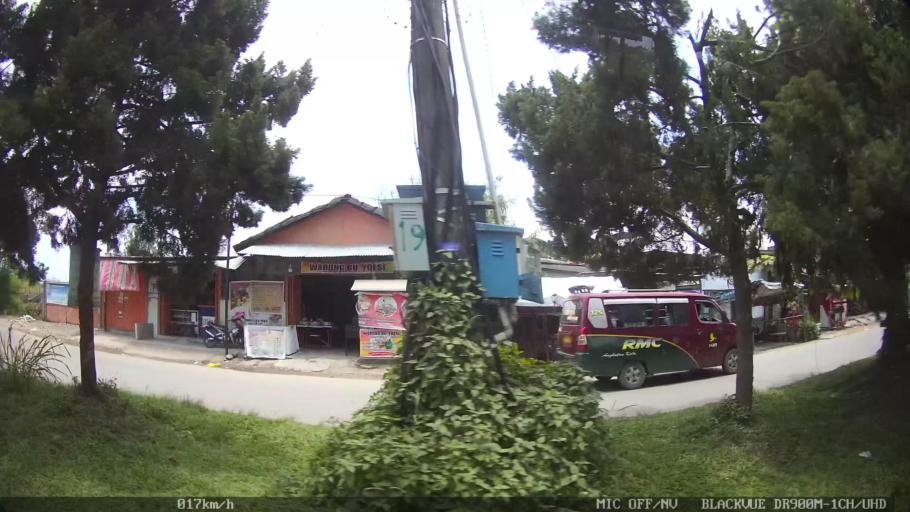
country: ID
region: North Sumatra
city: Labuhan Deli
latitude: 3.6892
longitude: 98.6932
